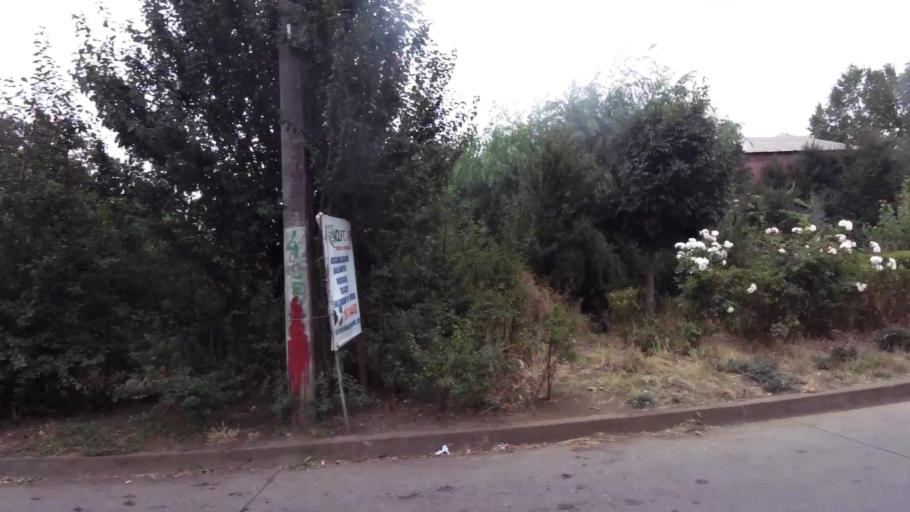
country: CL
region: Biobio
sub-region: Provincia de Concepcion
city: Concepcion
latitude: -36.8078
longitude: -73.0378
